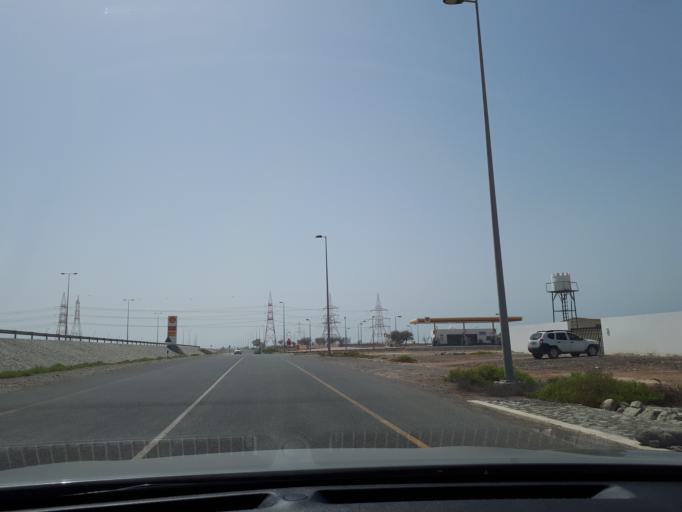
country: OM
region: Al Batinah
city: Barka'
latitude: 23.6996
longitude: 58.0092
